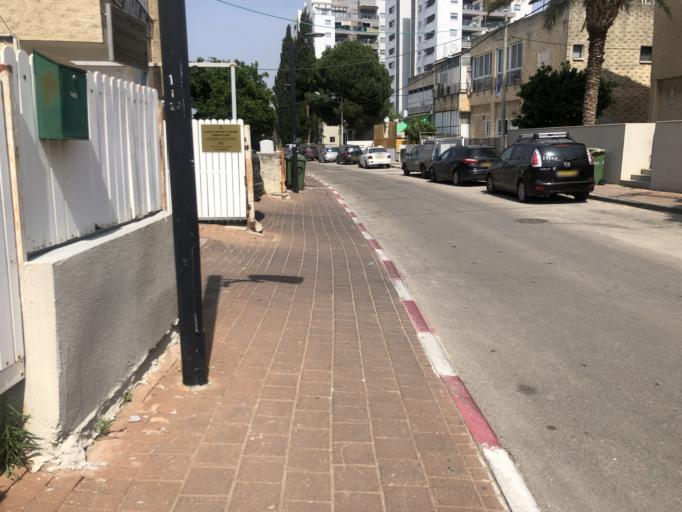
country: IL
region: Central District
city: Rosh Ha'Ayin
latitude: 32.0951
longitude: 34.9424
